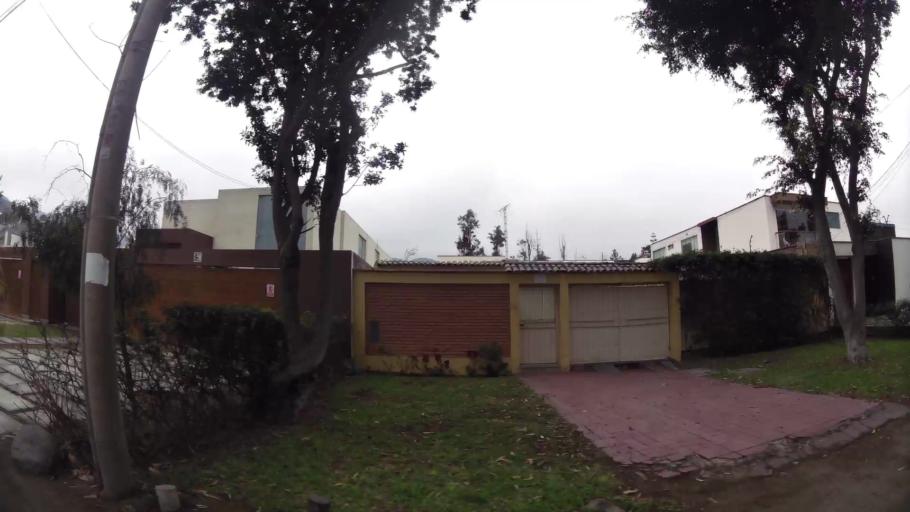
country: PE
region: Lima
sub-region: Lima
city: La Molina
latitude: -12.0776
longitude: -76.9162
